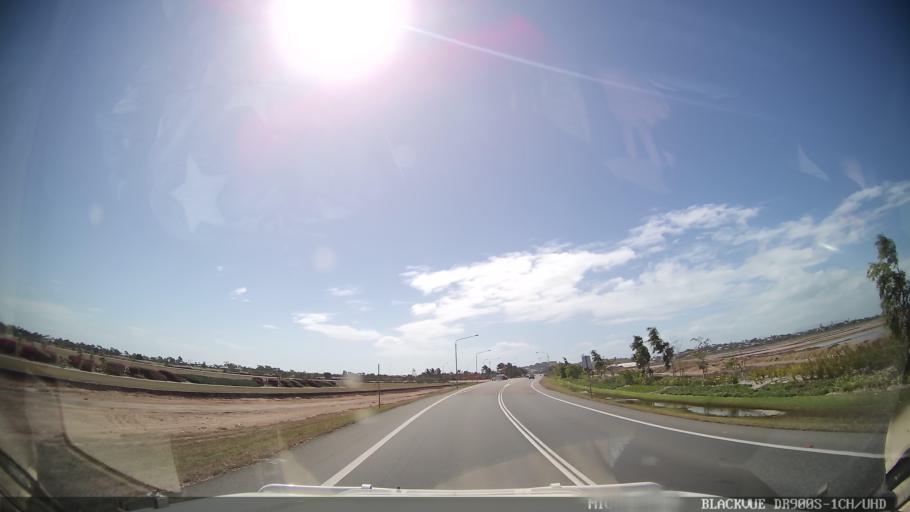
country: AU
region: Queensland
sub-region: Whitsunday
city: Bowen
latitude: -20.0165
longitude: 148.2198
